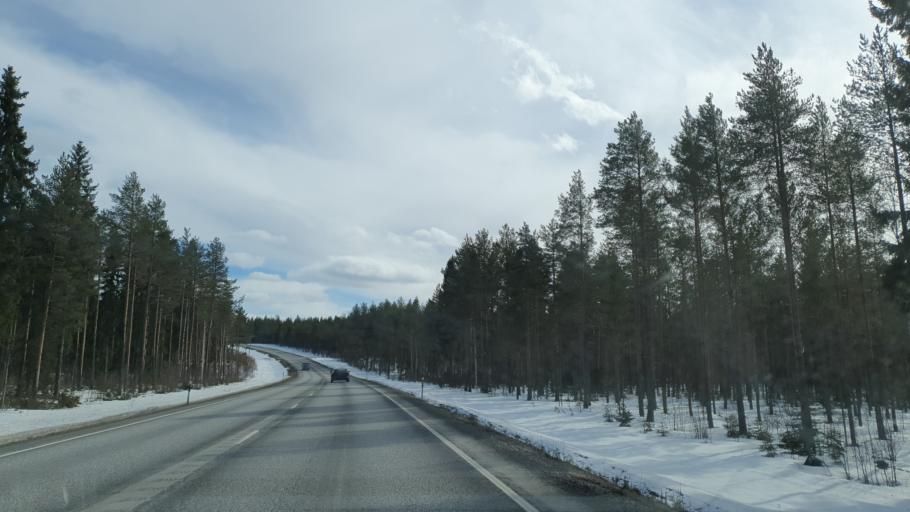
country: FI
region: Kainuu
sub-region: Kajaani
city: Paltamo
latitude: 64.3737
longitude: 28.0290
